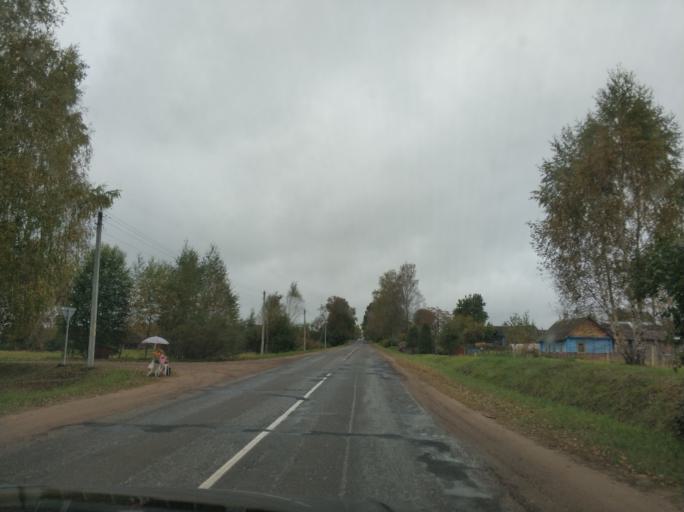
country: BY
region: Vitebsk
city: Polatsk
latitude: 55.4290
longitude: 29.0031
